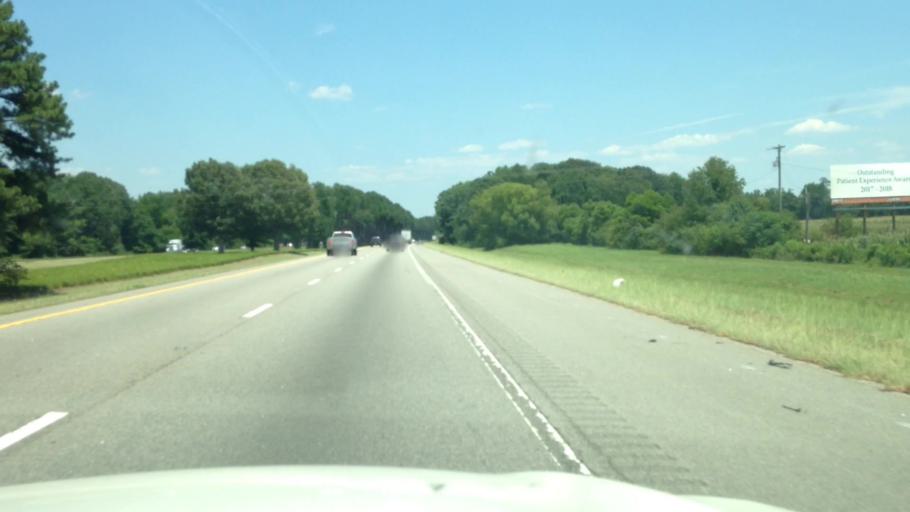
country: US
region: North Carolina
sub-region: Robeson County
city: Rowland
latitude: 34.5294
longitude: -79.2650
